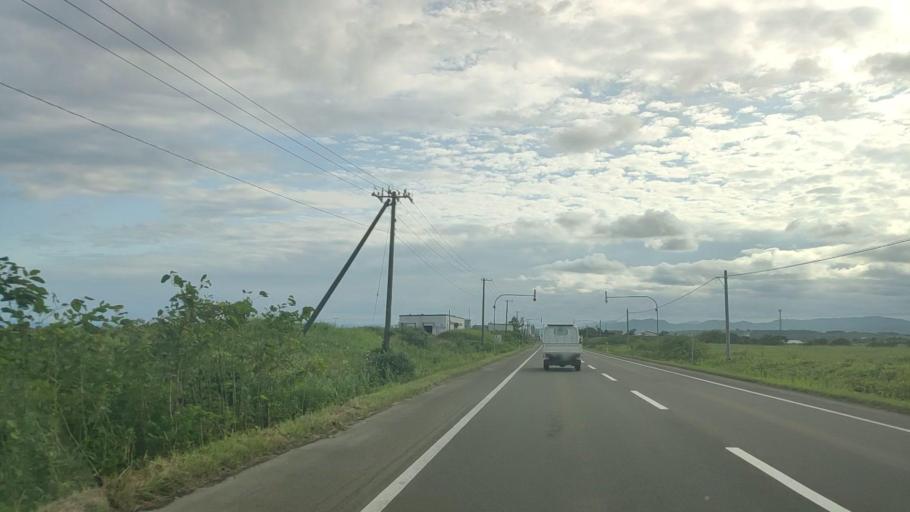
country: JP
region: Hokkaido
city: Niseko Town
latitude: 42.5326
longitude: 140.3984
